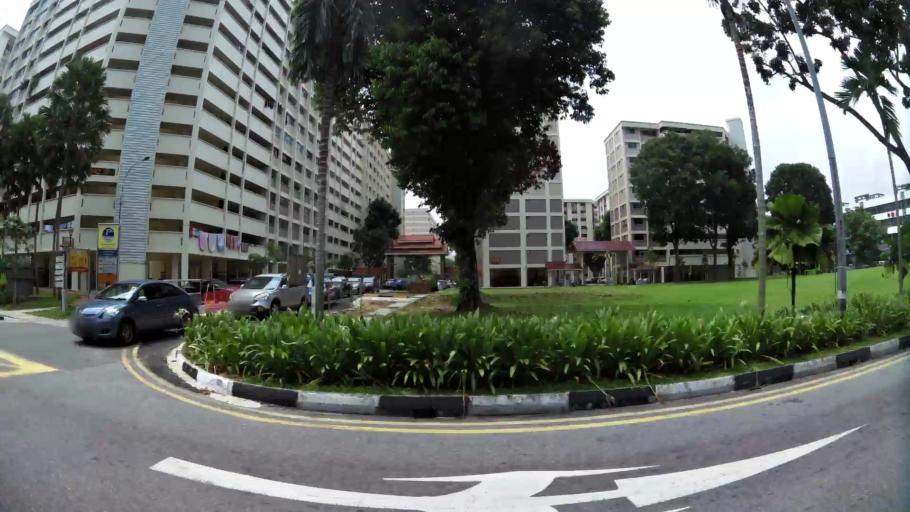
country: SG
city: Singapore
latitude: 1.3363
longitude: 103.9137
